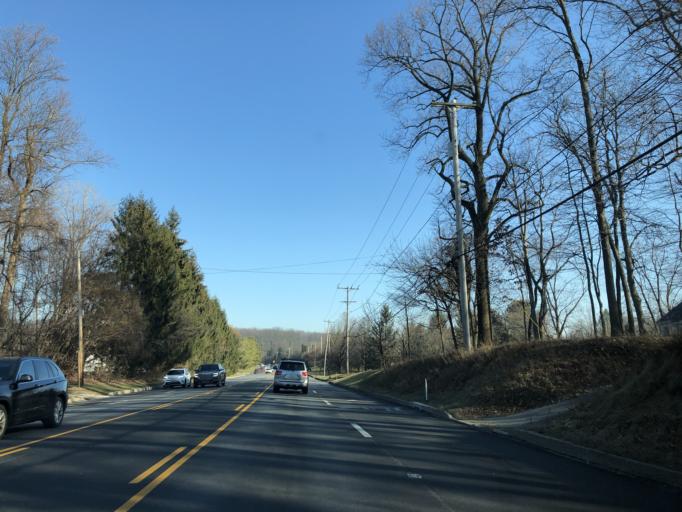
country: US
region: Pennsylvania
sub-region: Chester County
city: Downingtown
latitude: 40.0335
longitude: -75.6768
